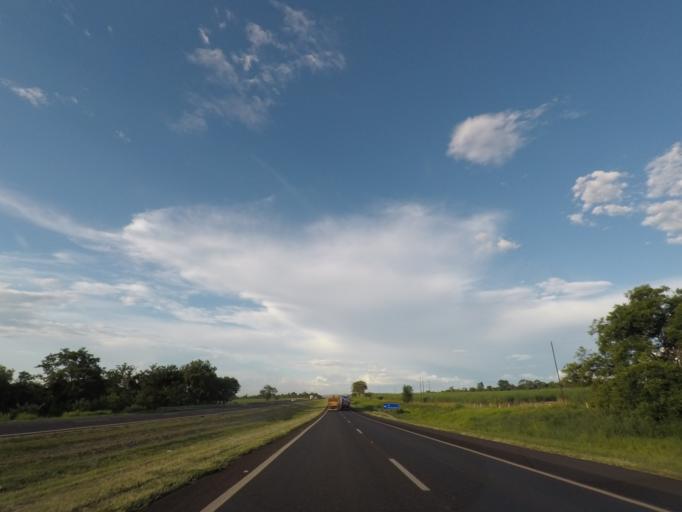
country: BR
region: Sao Paulo
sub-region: Ituverava
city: Ituverava
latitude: -20.3137
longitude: -47.8017
